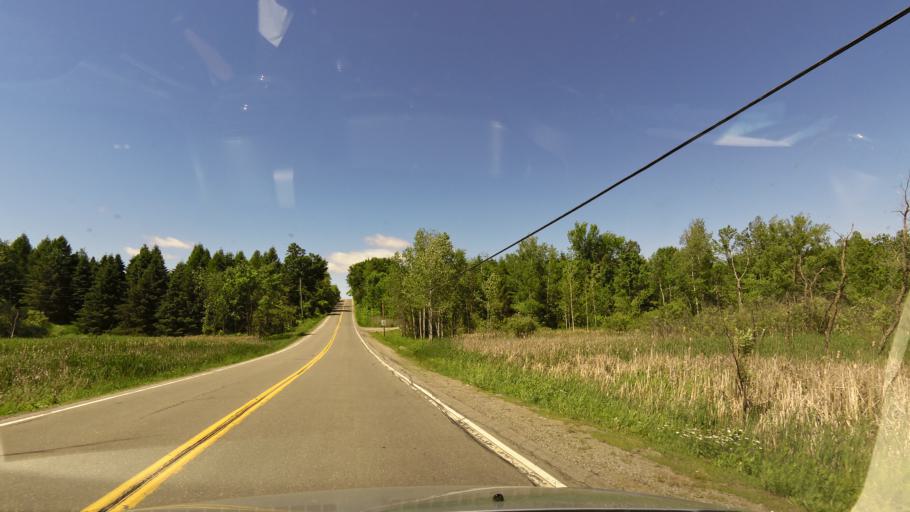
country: CA
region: Ontario
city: Newmarket
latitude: 43.9576
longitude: -79.5362
